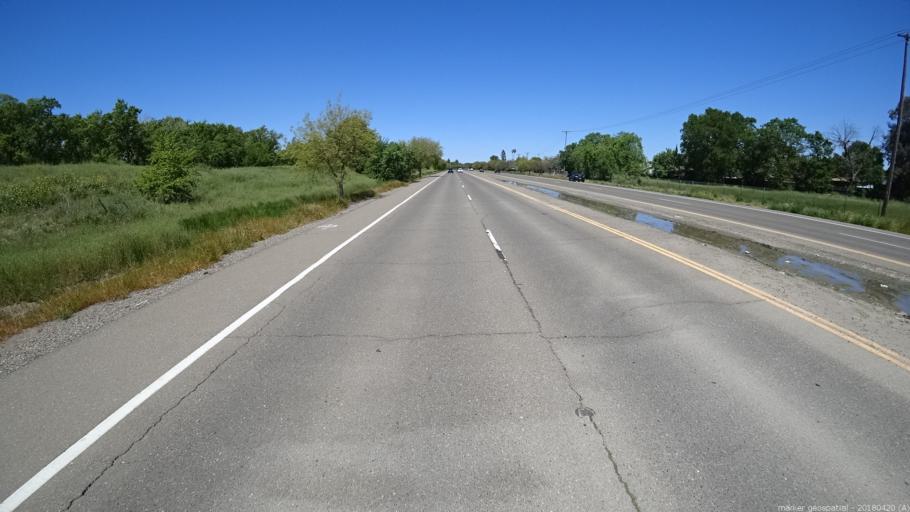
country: US
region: California
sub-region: Sacramento County
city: Parkway
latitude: 38.4840
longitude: -121.5056
